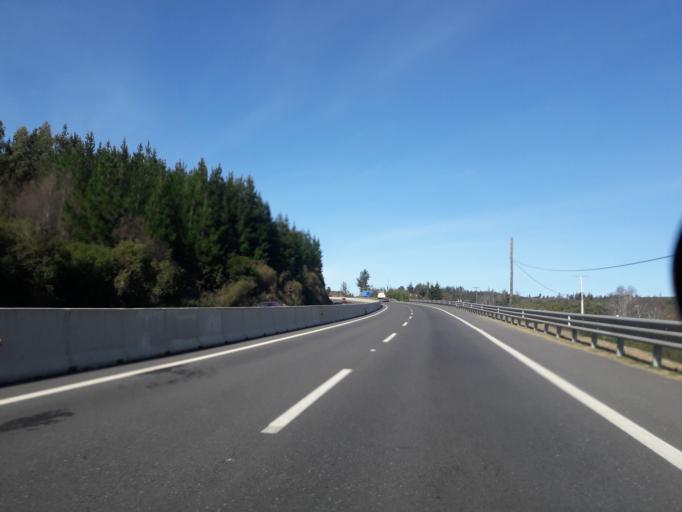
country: CL
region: Biobio
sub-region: Provincia de Concepcion
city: Chiguayante
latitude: -36.9225
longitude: -72.7729
